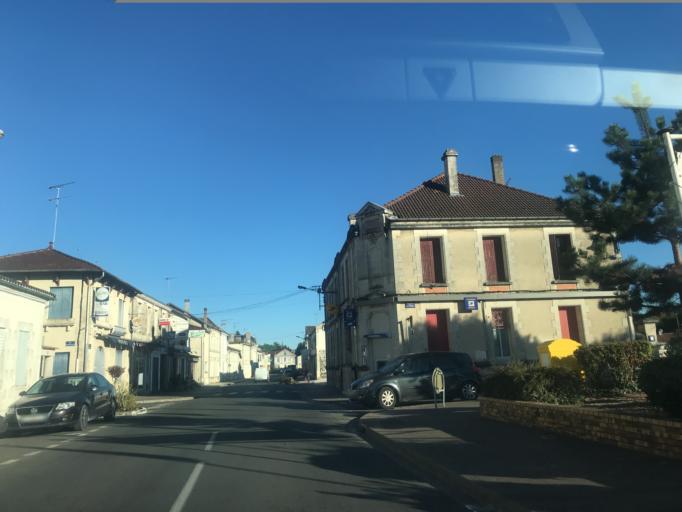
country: FR
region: Poitou-Charentes
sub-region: Departement de la Charente-Maritime
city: Saint-Aigulin
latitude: 45.1582
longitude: -0.0116
